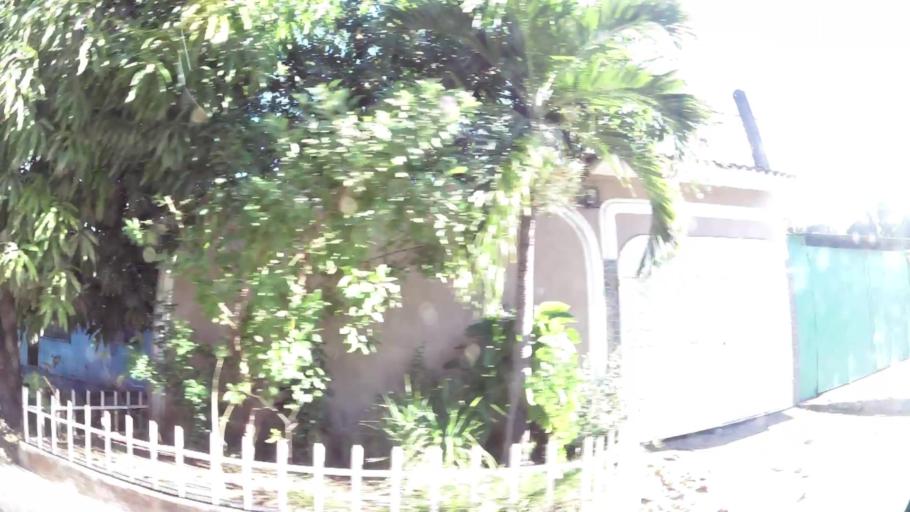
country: SV
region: Sonsonate
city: Sonsonate
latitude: 13.7151
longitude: -89.7177
